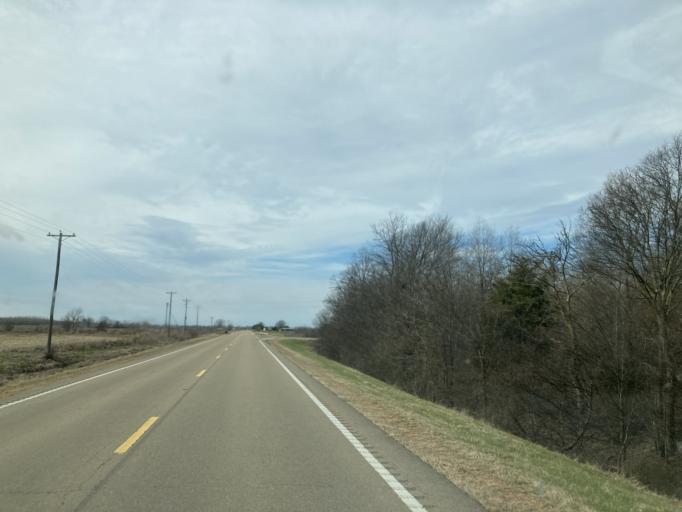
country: US
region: Mississippi
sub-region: Humphreys County
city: Belzoni
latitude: 33.1826
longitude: -90.6309
